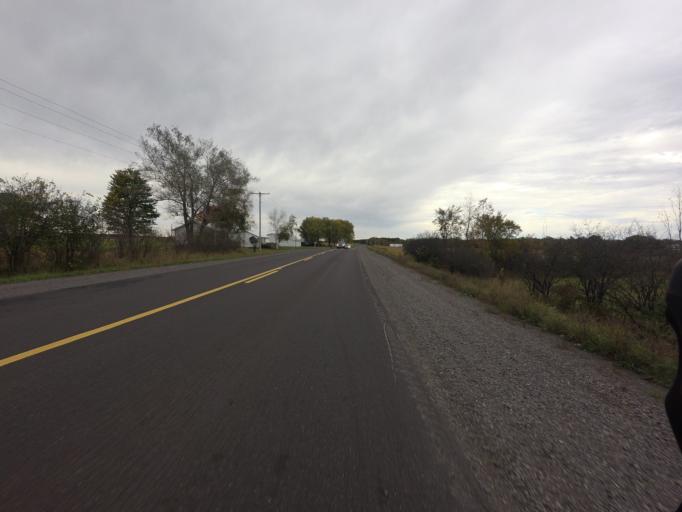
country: CA
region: Ontario
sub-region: Lanark County
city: Smiths Falls
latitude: 44.9870
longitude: -75.7858
